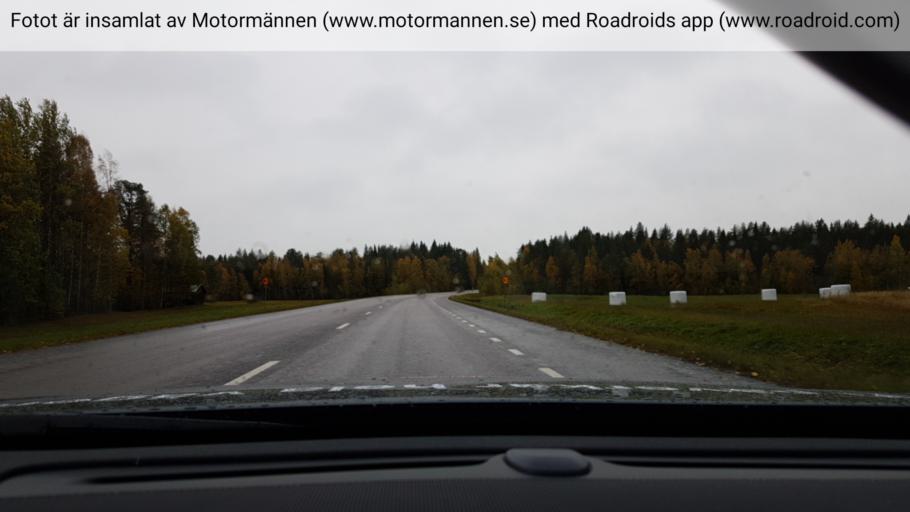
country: SE
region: Norrbotten
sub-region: Lulea Kommun
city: Gammelstad
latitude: 65.5852
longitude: 22.0246
